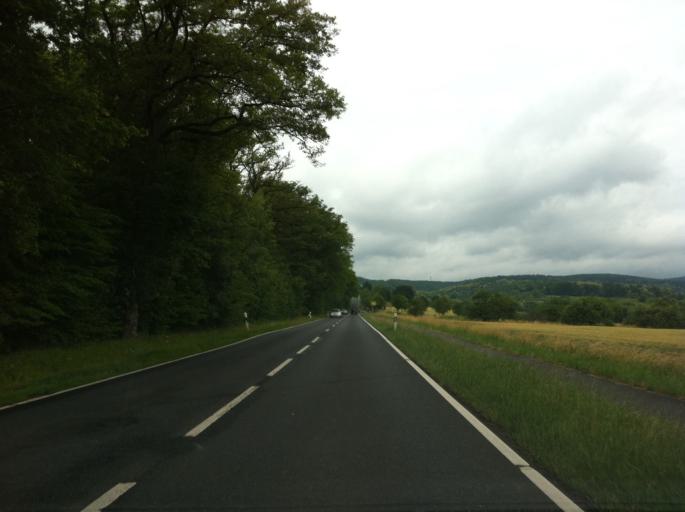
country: DE
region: Hesse
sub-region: Regierungsbezirk Darmstadt
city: Bad Soden am Taunus
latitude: 50.1531
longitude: 8.5131
